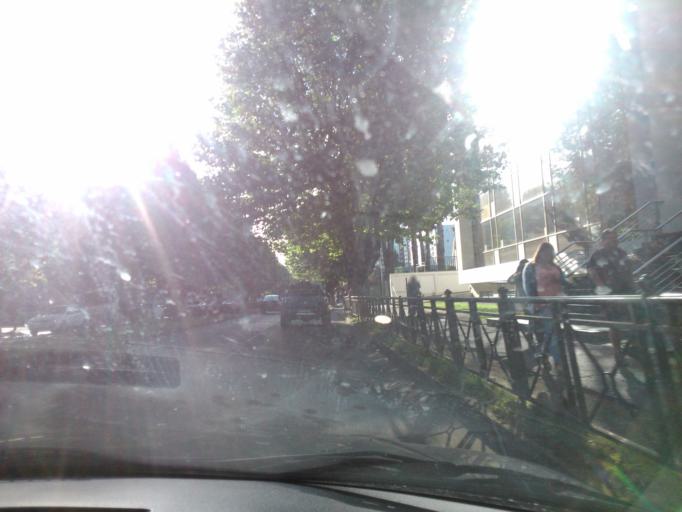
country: CL
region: Araucania
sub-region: Provincia de Cautin
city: Temuco
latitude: -38.7360
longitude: -72.6058
